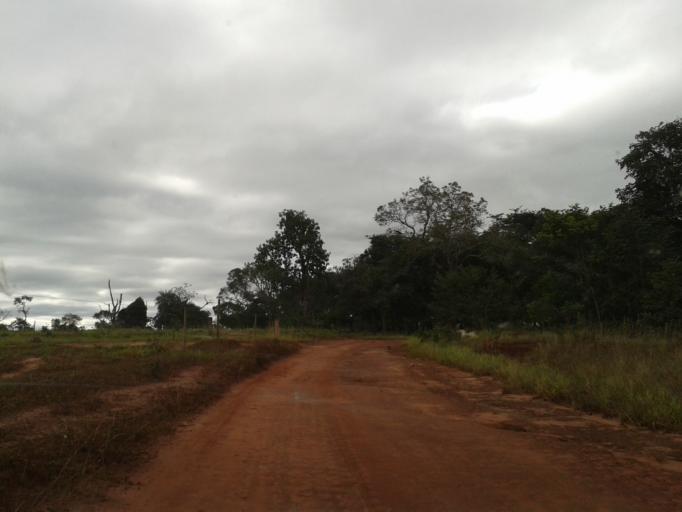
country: BR
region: Minas Gerais
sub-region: Campina Verde
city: Campina Verde
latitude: -19.5080
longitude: -49.6615
